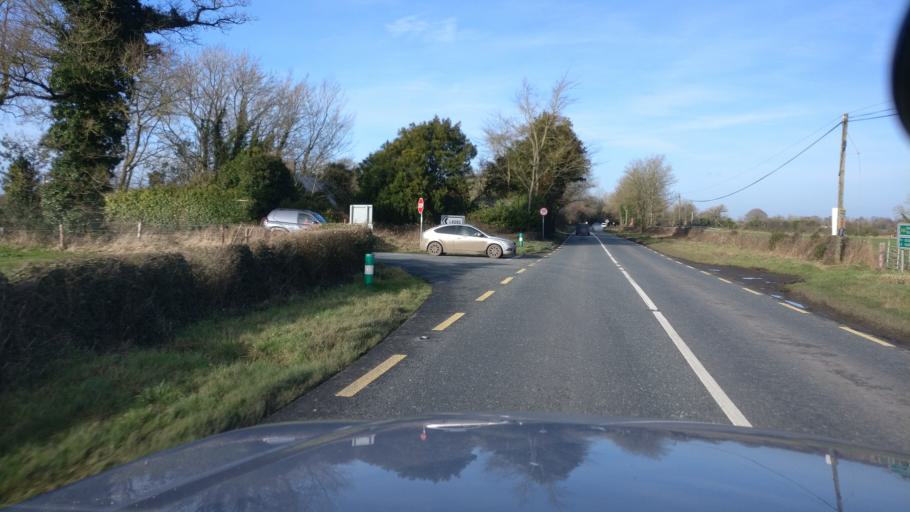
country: IE
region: Leinster
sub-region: Laois
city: Mountmellick
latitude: 53.1522
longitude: -7.3700
